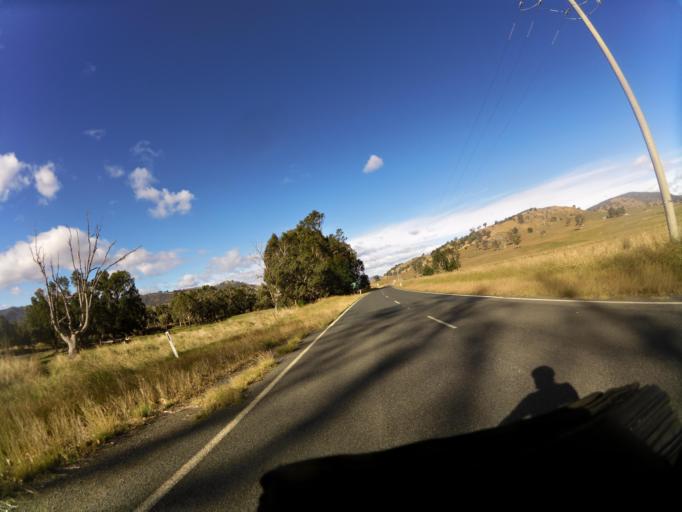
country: AU
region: New South Wales
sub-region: Greater Hume Shire
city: Holbrook
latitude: -35.9640
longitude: 147.7397
